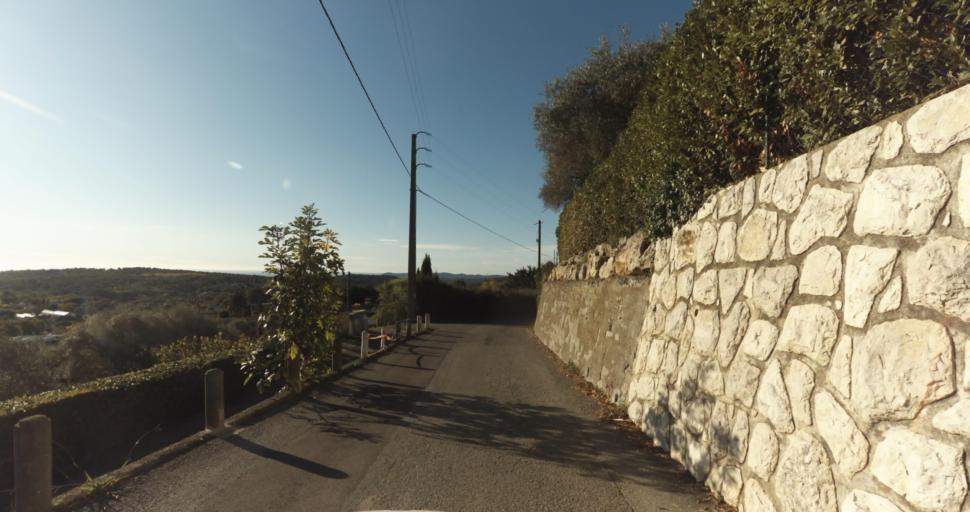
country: FR
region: Provence-Alpes-Cote d'Azur
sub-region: Departement des Alpes-Maritimes
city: Vence
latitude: 43.7276
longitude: 7.0850
